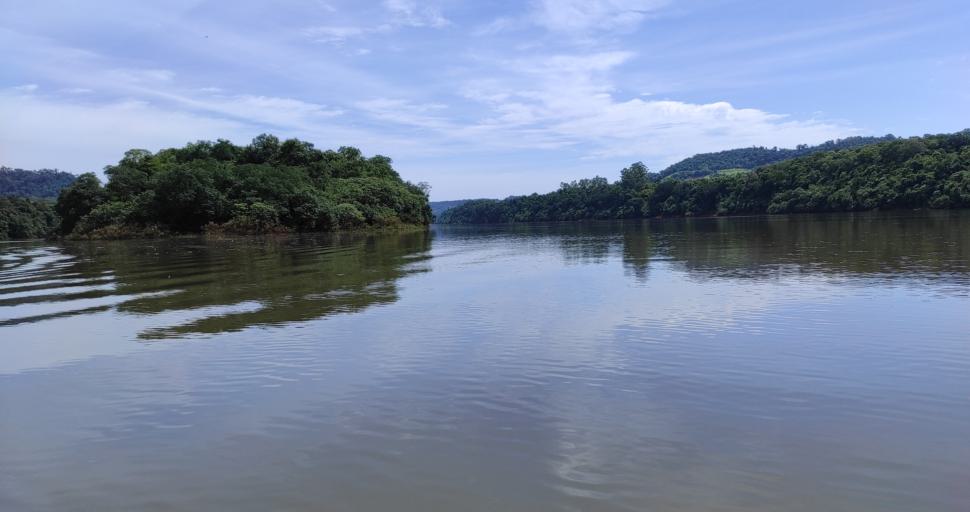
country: AR
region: Misiones
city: El Soberbio
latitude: -27.2898
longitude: -54.1940
